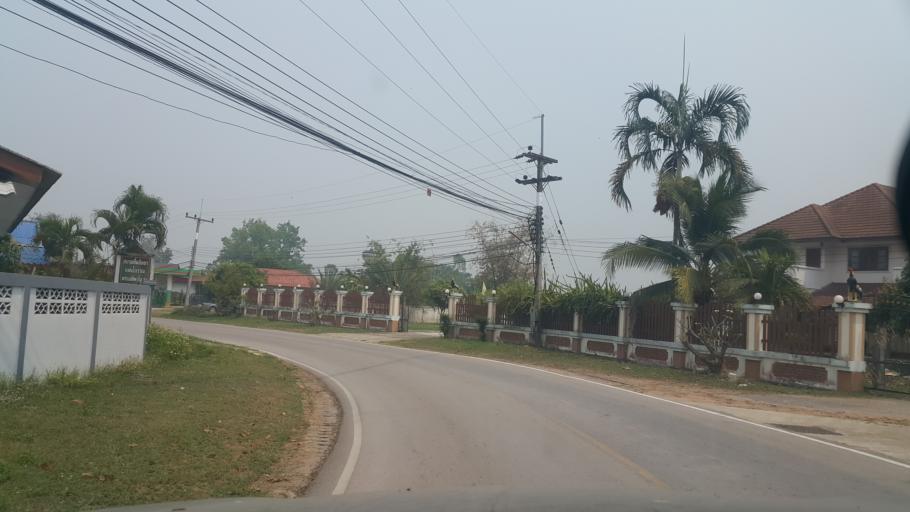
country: TH
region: Lampang
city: Hang Chat
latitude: 18.2710
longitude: 99.2494
